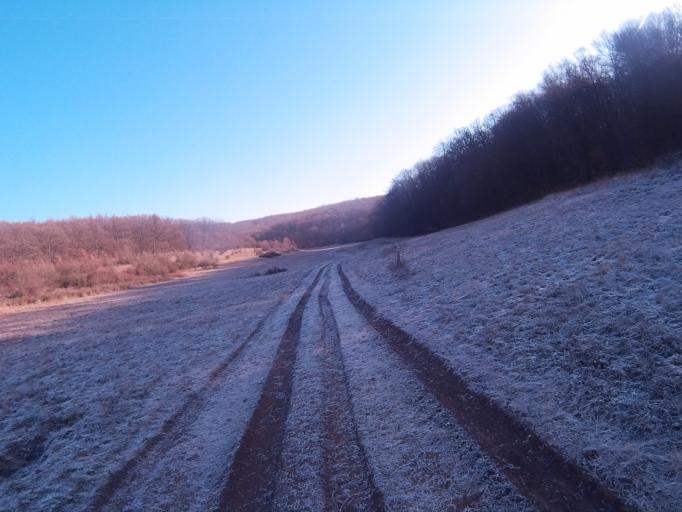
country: HU
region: Borsod-Abauj-Zemplen
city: Rudabanya
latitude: 48.4929
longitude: 20.5707
